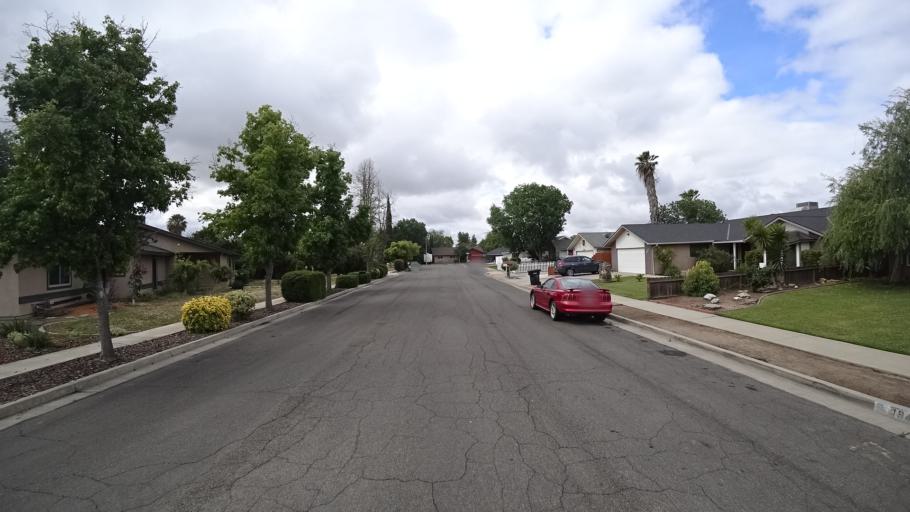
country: US
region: California
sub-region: Kings County
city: Hanford
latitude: 36.3463
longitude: -119.6613
